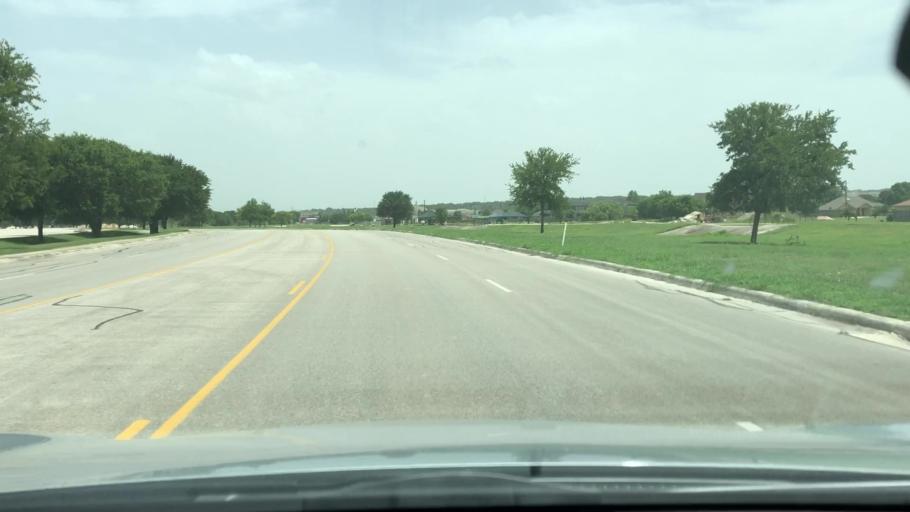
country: US
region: Texas
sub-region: Bexar County
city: Selma
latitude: 29.5852
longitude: -98.3235
